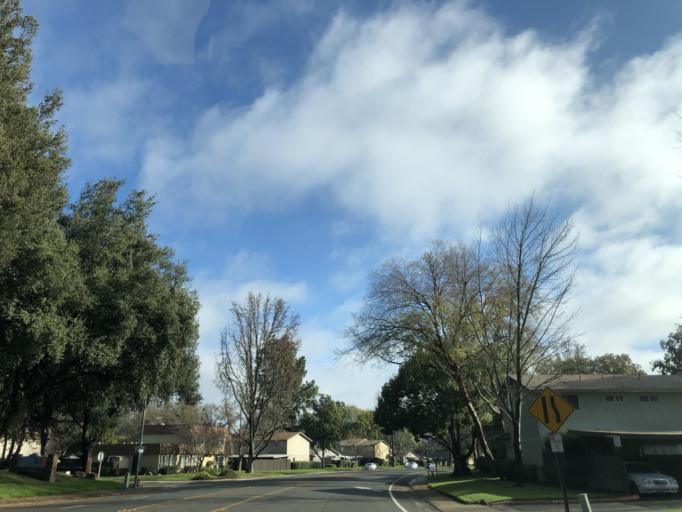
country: US
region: California
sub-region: Sacramento County
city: Rosemont
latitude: 38.5643
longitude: -121.3774
